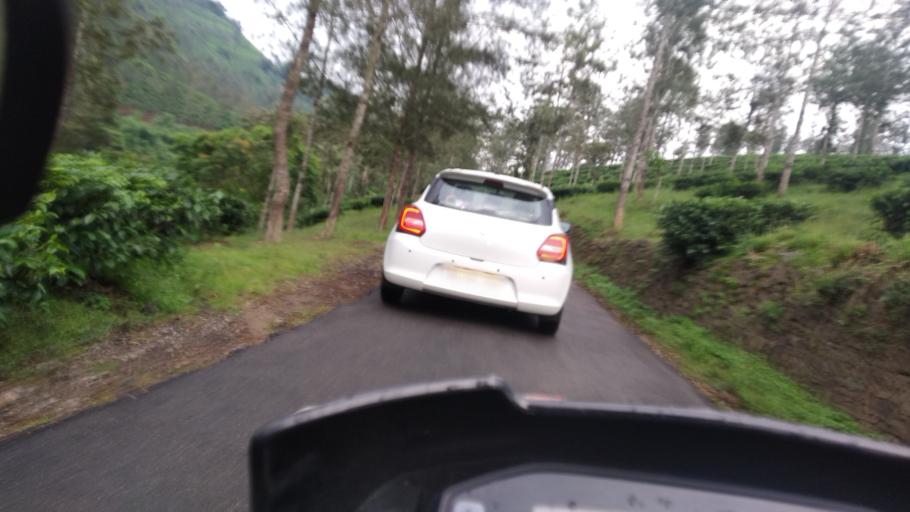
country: IN
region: Tamil Nadu
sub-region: Theni
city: Gudalur
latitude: 9.5649
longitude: 77.0776
